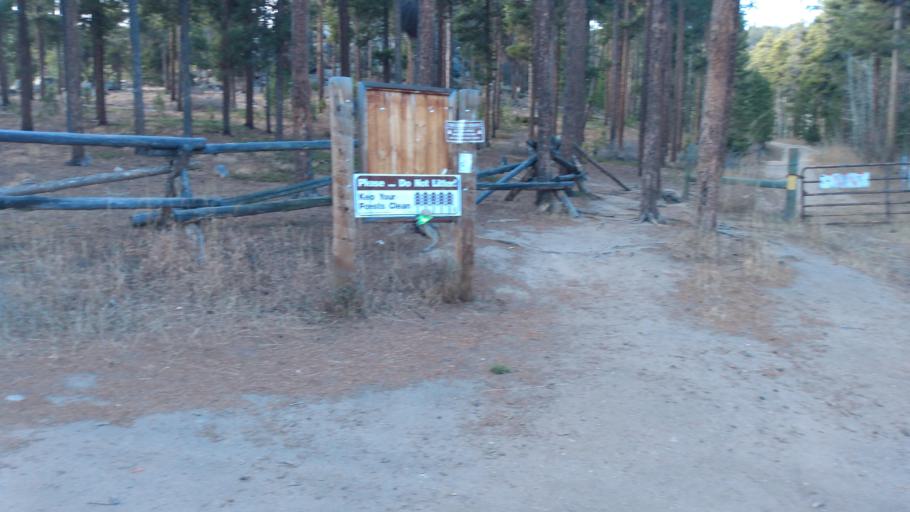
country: US
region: Colorado
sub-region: Boulder County
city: Nederland
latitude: 39.9573
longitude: -105.4472
